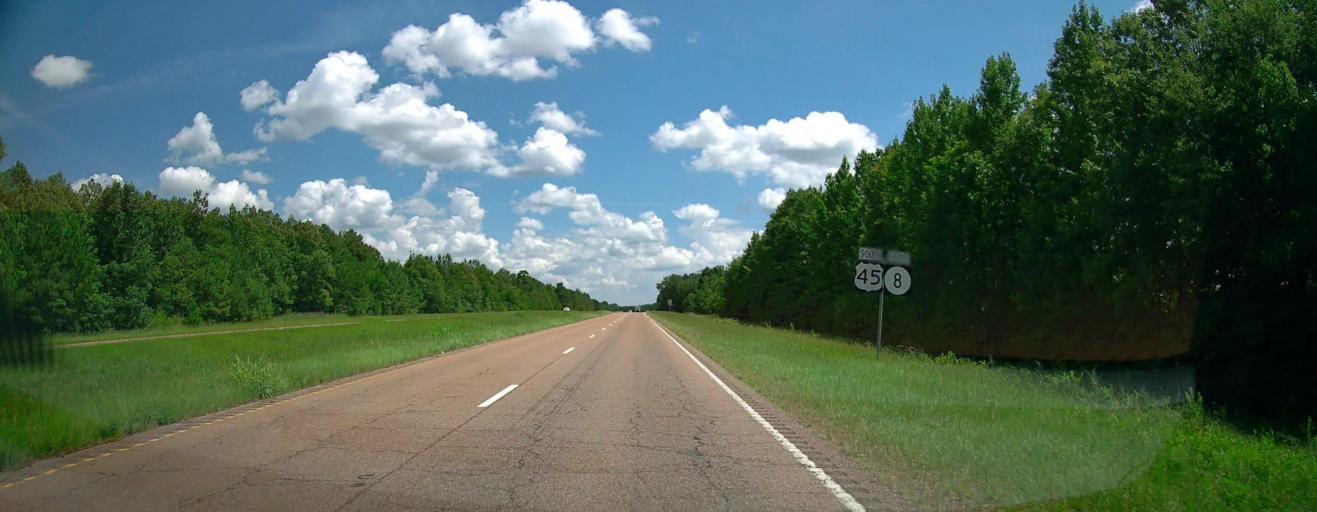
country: US
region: Mississippi
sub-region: Monroe County
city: Aberdeen
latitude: 33.8333
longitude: -88.5886
